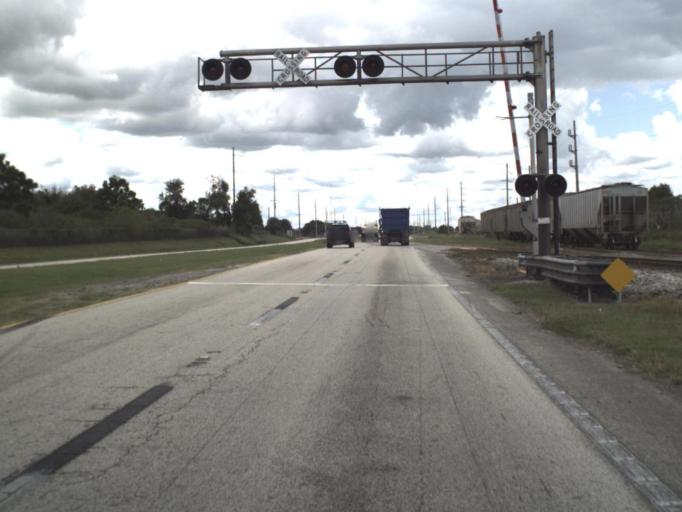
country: US
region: Florida
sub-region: Polk County
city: Bartow
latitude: 27.8976
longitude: -81.8761
